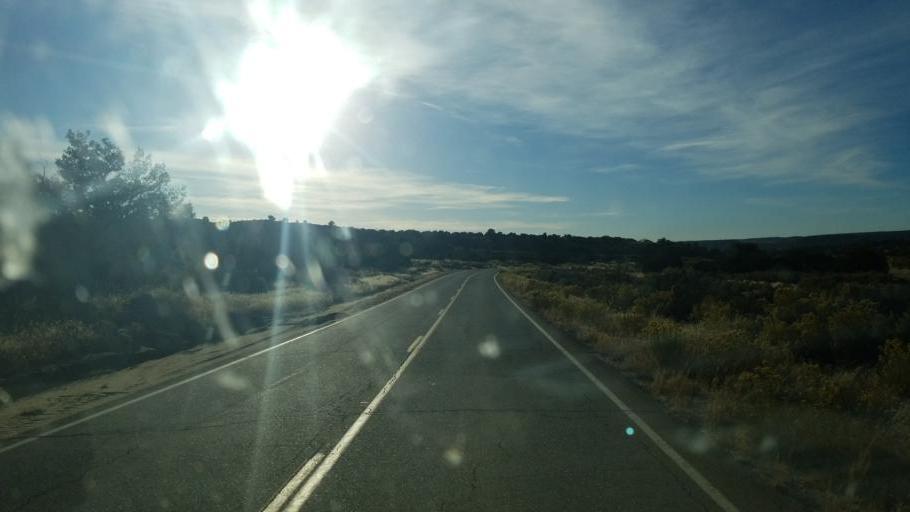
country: US
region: New Mexico
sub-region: San Juan County
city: Bloomfield
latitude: 36.7327
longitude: -107.7683
